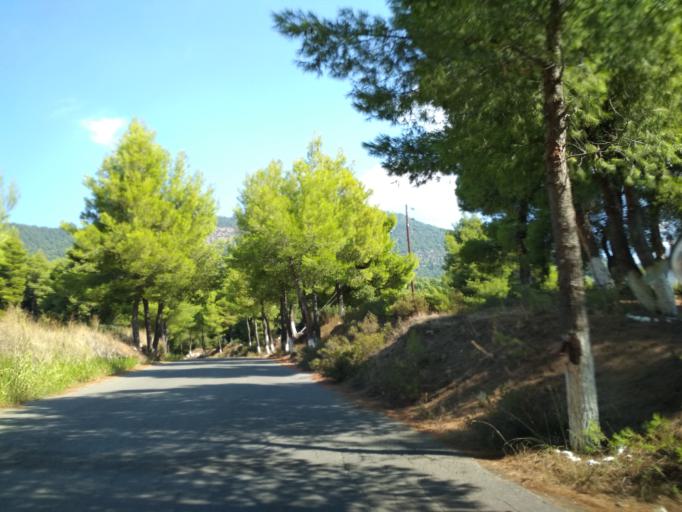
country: GR
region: Central Greece
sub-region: Nomos Evvoias
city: Roviai
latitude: 38.8220
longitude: 23.2505
